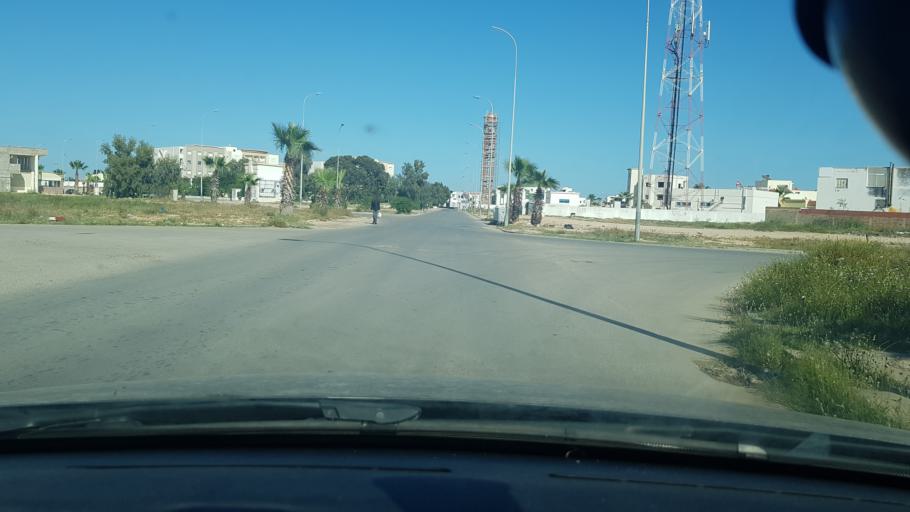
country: TN
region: Safaqis
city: Al Qarmadah
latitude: 34.8275
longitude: 10.7560
